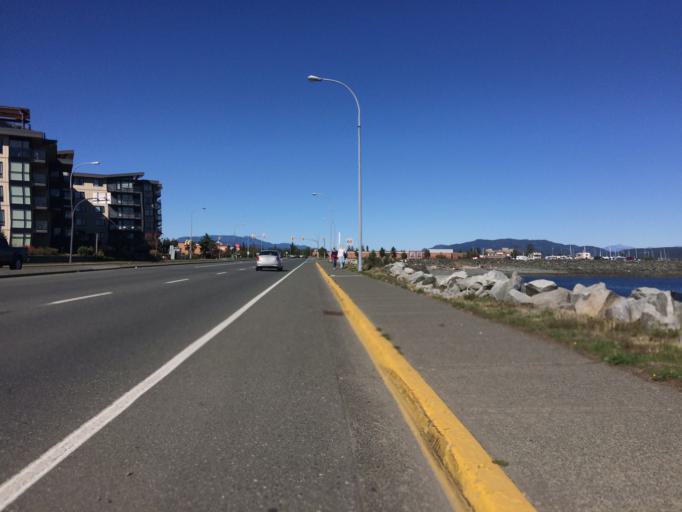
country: CA
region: British Columbia
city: Campbell River
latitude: 50.0288
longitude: -125.2435
